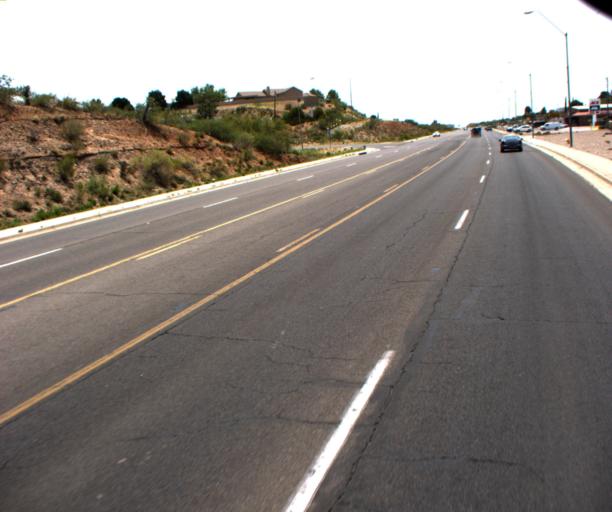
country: US
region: Arizona
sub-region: Gila County
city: Globe
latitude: 33.3882
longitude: -110.7611
